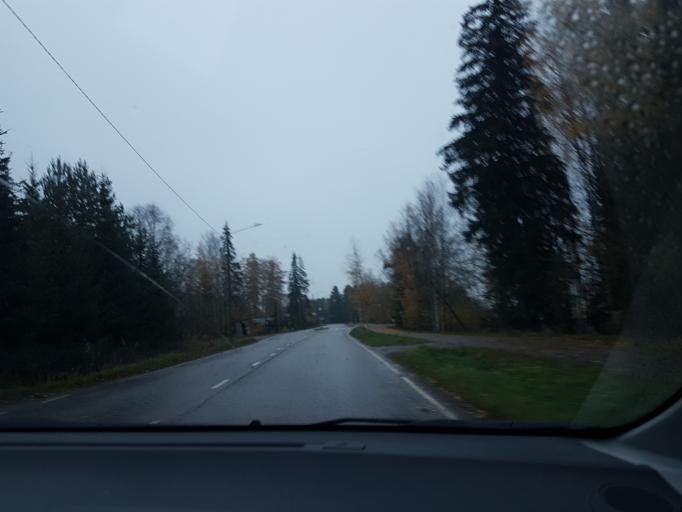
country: FI
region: Uusimaa
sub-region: Helsinki
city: Jaervenpaeae
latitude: 60.5662
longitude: 25.1393
